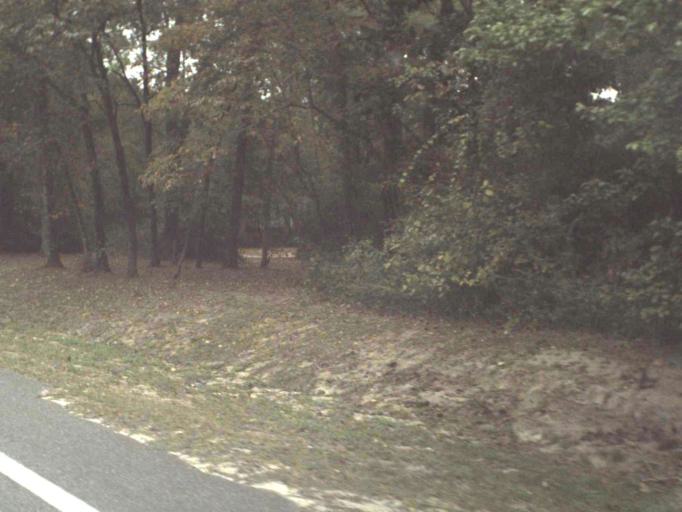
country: US
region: Florida
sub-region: Wakulla County
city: Crawfordville
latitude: 30.1114
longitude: -84.3820
